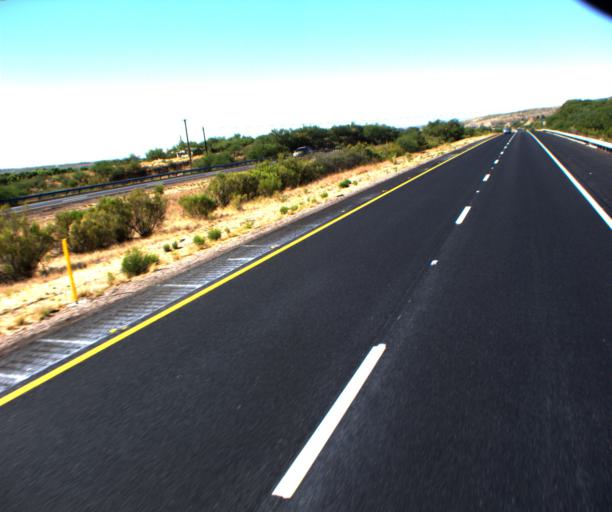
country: US
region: Arizona
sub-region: Santa Cruz County
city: Tubac
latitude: 31.5978
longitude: -111.0525
